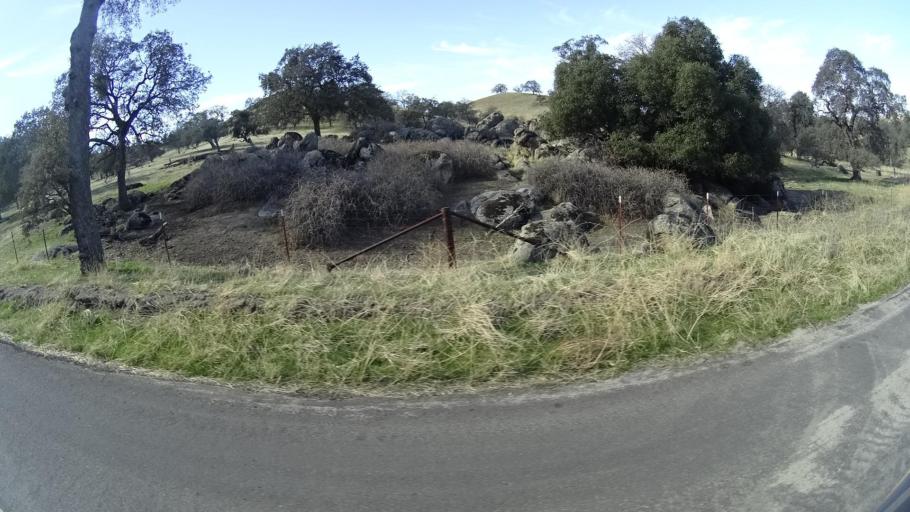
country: US
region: California
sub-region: Tulare County
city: Richgrove
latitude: 35.6696
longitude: -118.8497
